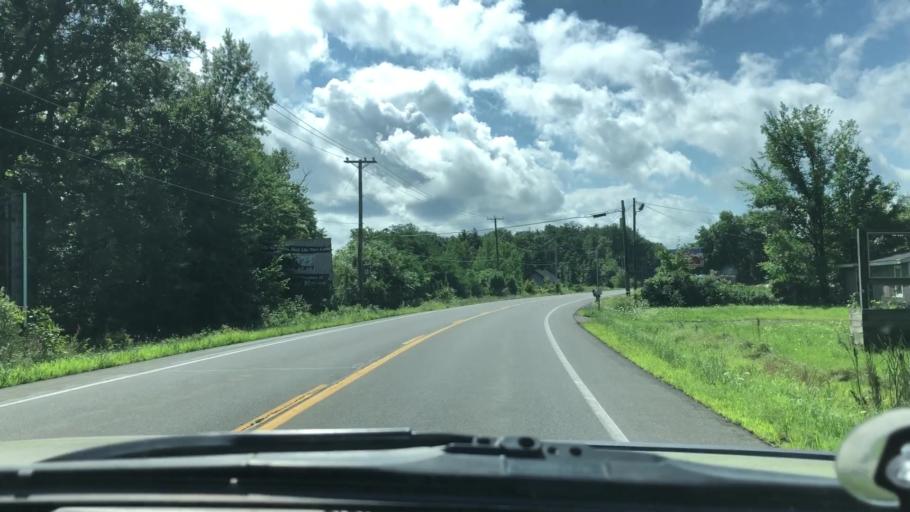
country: US
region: New York
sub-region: Greene County
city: Cairo
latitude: 42.2903
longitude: -73.9862
